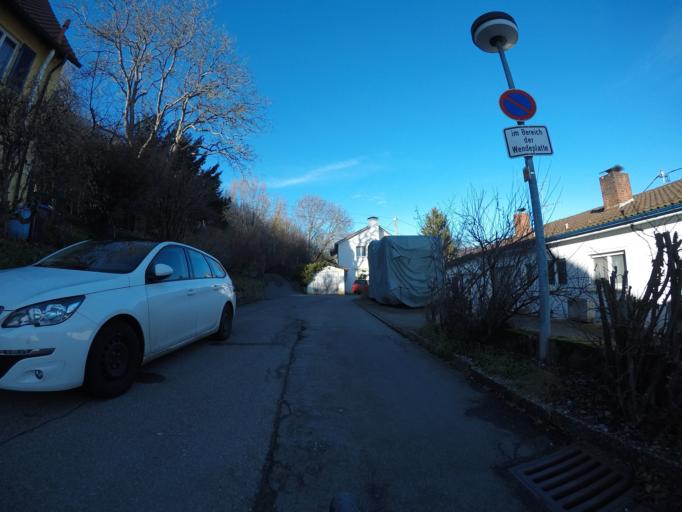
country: DE
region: Baden-Wuerttemberg
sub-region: Tuebingen Region
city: Pfullingen
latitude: 48.4361
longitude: 9.2529
